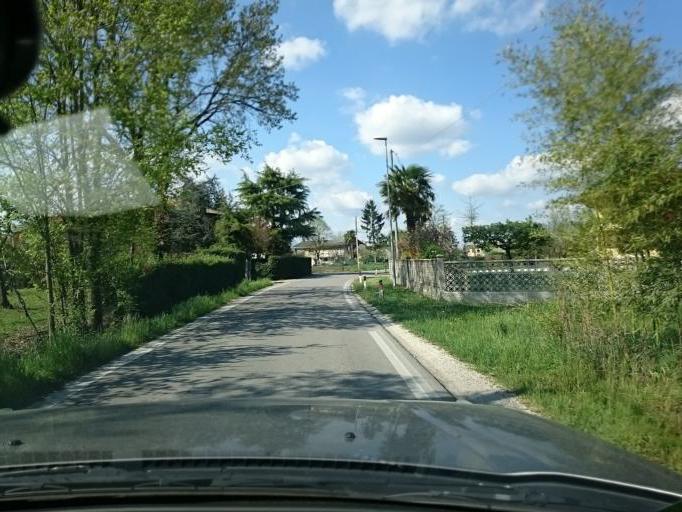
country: IT
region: Veneto
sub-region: Provincia di Padova
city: Pionca
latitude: 45.4584
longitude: 11.9757
